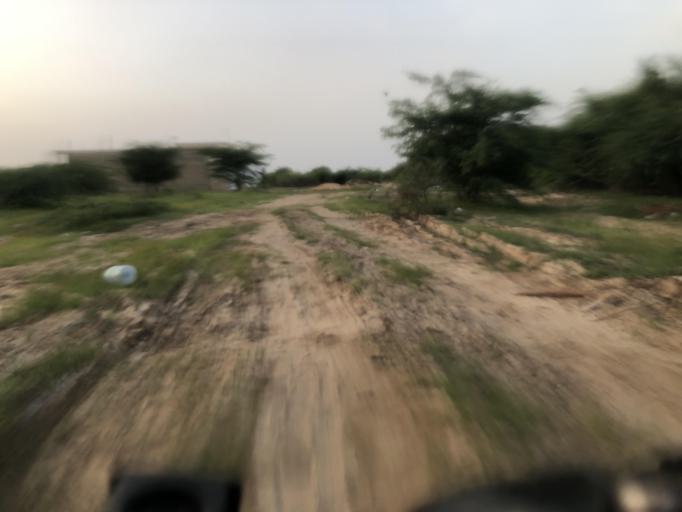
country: SN
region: Saint-Louis
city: Saint-Louis
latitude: 16.0563
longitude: -16.4318
